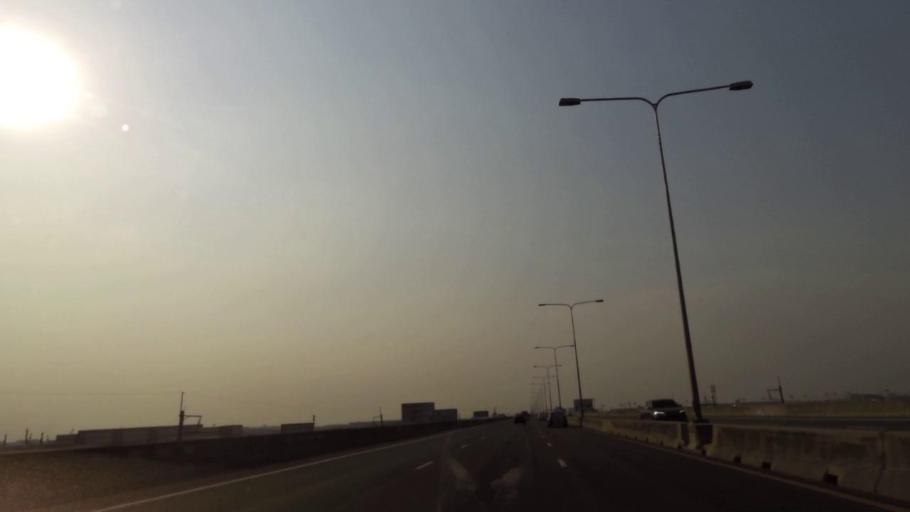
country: TH
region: Samut Prakan
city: Bang Bo District
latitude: 13.5973
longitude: 100.8000
